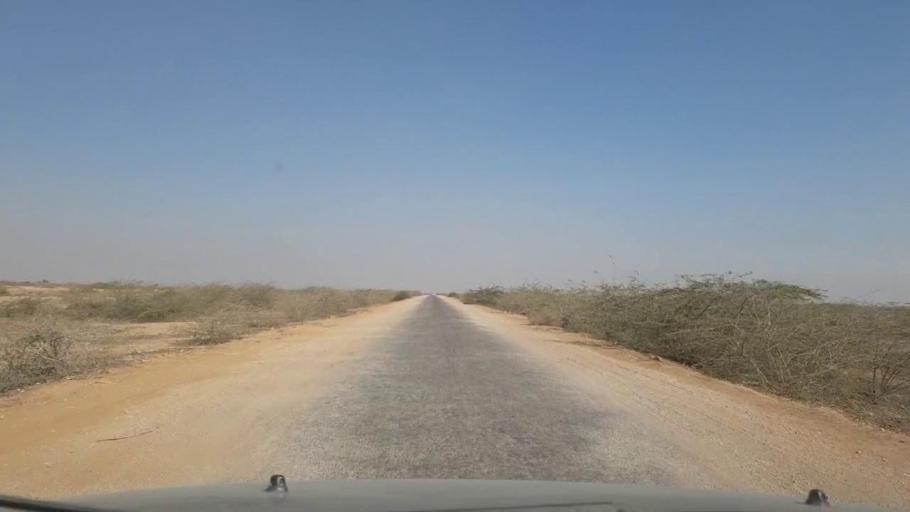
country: PK
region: Sindh
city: Thatta
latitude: 24.8964
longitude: 67.9179
